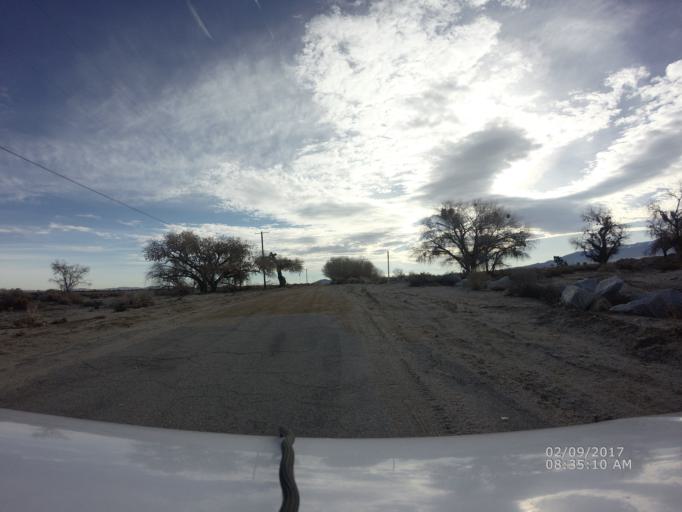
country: US
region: California
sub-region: Los Angeles County
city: Lake Los Angeles
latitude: 34.5580
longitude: -117.8542
